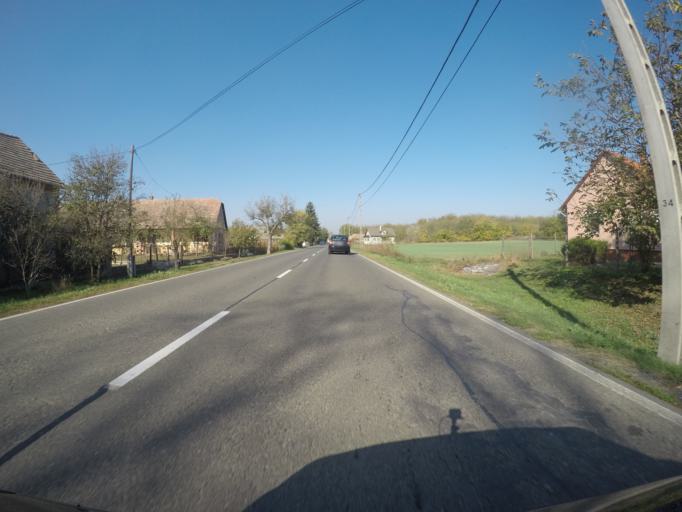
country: HU
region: Tolna
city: Szedres
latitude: 46.5076
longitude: 18.6671
